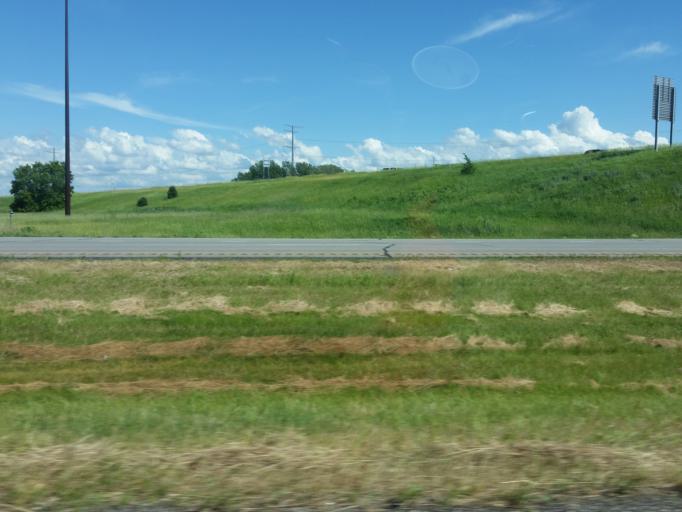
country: US
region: Minnesota
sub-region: Stearns County
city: Saint Augusta
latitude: 45.4988
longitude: -94.2398
